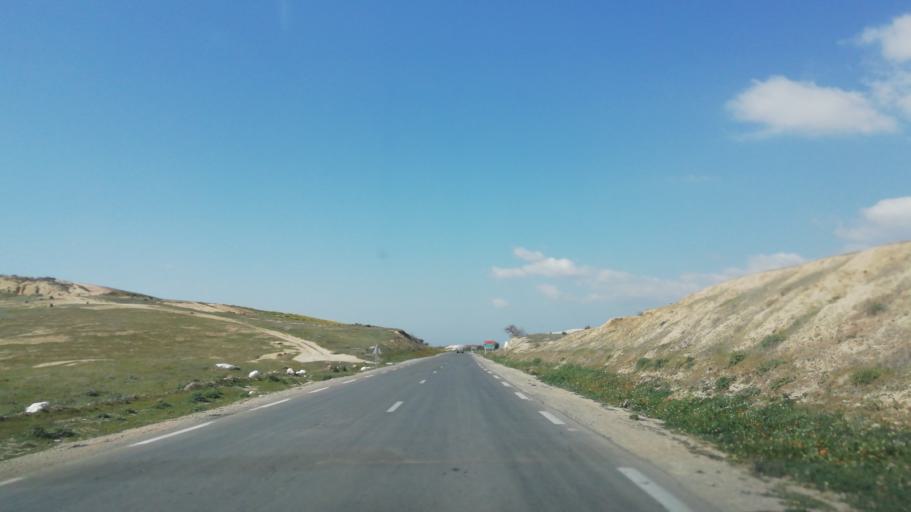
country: DZ
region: Mascara
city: Mascara
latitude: 35.5417
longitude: 0.0931
